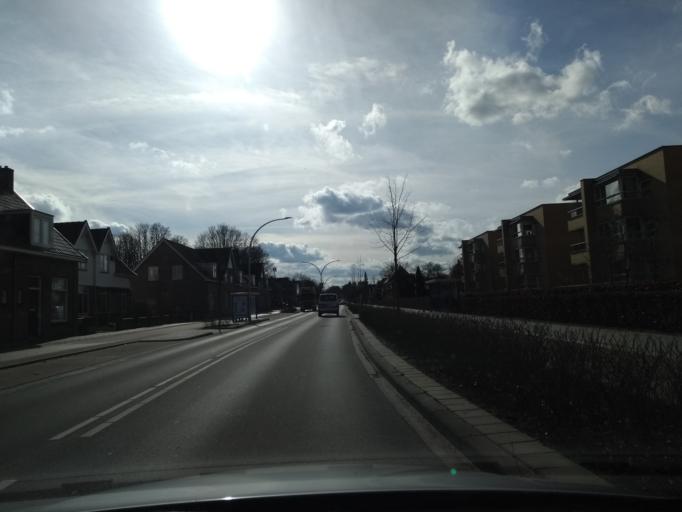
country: NL
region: Overijssel
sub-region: Gemeente Hengelo
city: Hengelo
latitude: 52.2576
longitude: 6.7762
